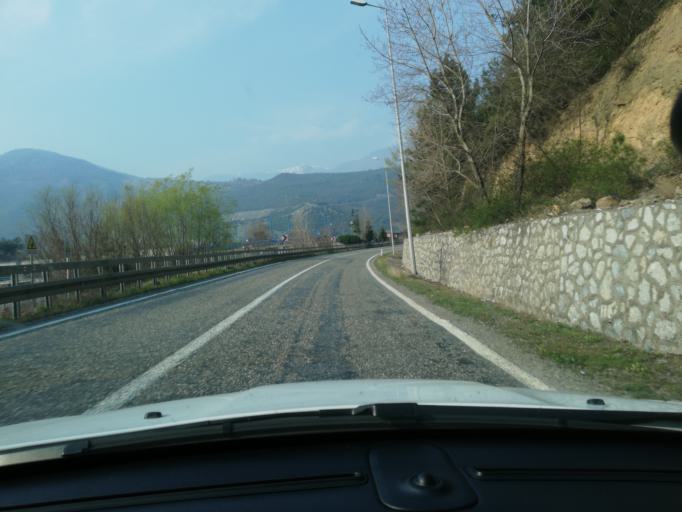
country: TR
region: Karabuk
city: Karabuk
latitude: 41.1565
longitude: 32.5419
